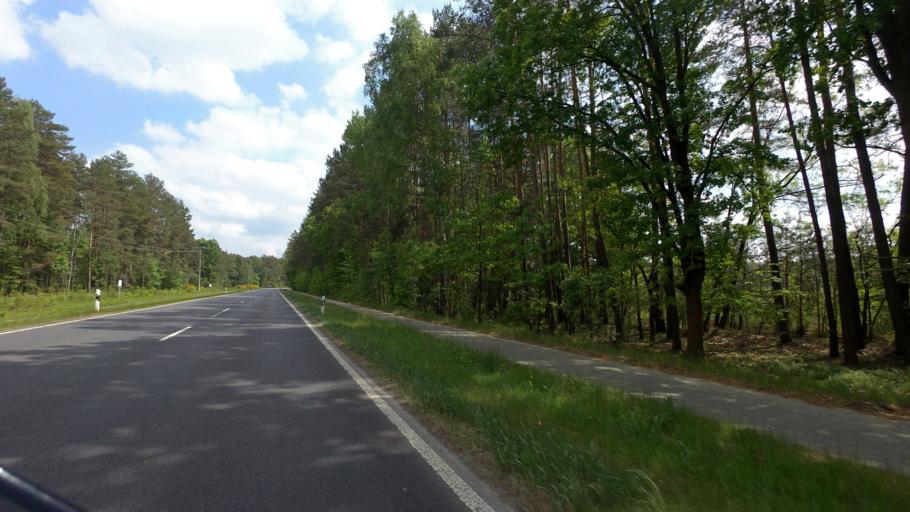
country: DE
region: Saxony
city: Weisskeissel
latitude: 51.4691
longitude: 14.7329
